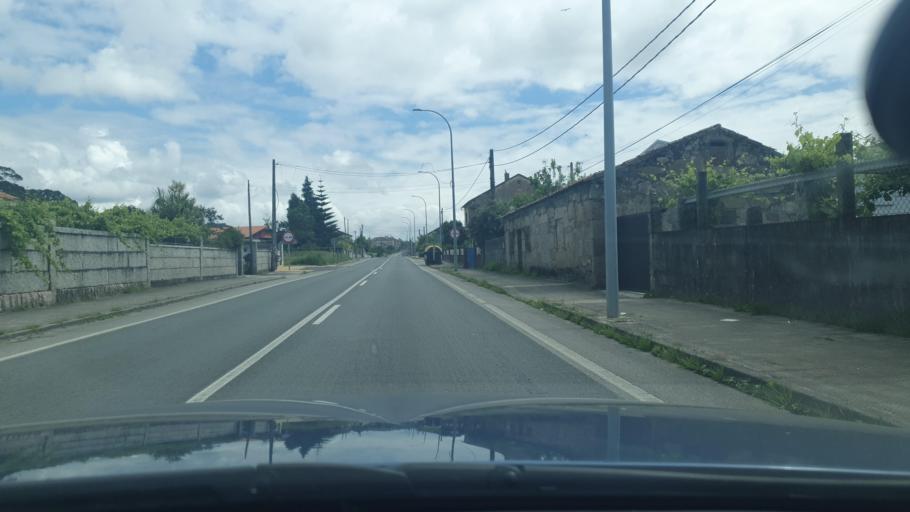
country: ES
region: Galicia
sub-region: Provincia de Pontevedra
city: Cambados
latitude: 42.4982
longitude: -8.8031
